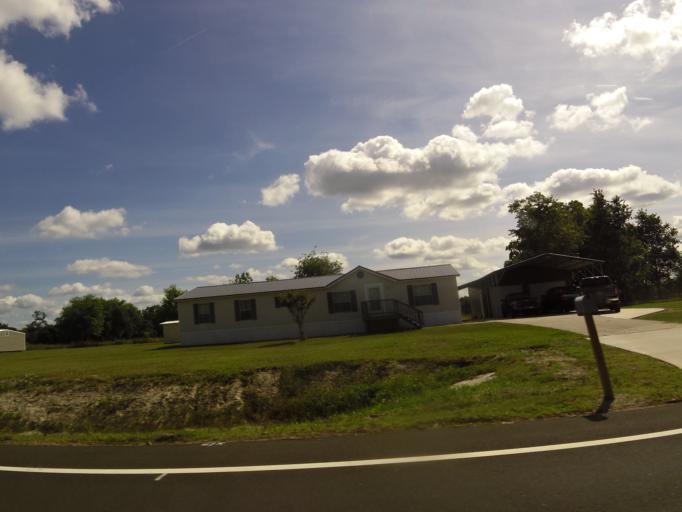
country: US
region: Florida
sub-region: Nassau County
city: Callahan
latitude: 30.6005
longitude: -81.8657
